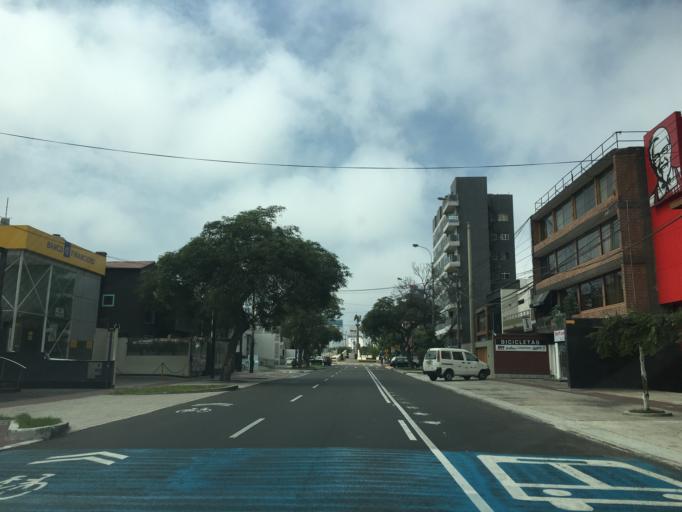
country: PE
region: Lima
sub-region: Lima
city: San Isidro
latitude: -12.1090
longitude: -77.0382
